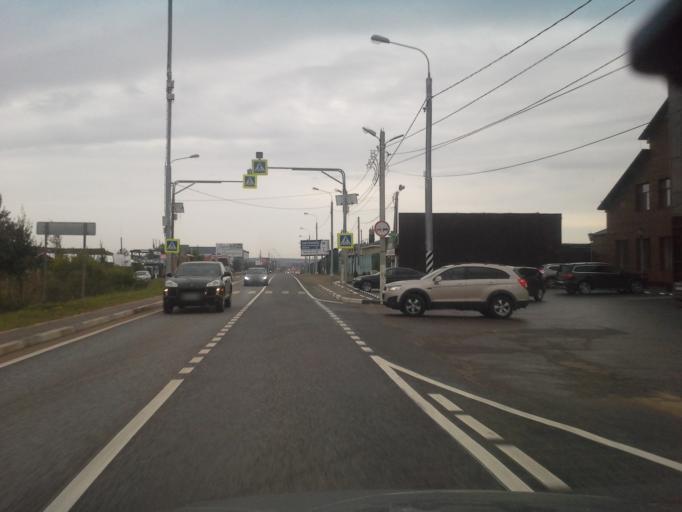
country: RU
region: Moskovskaya
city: Gorki Vtoryye
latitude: 55.7536
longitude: 37.1220
